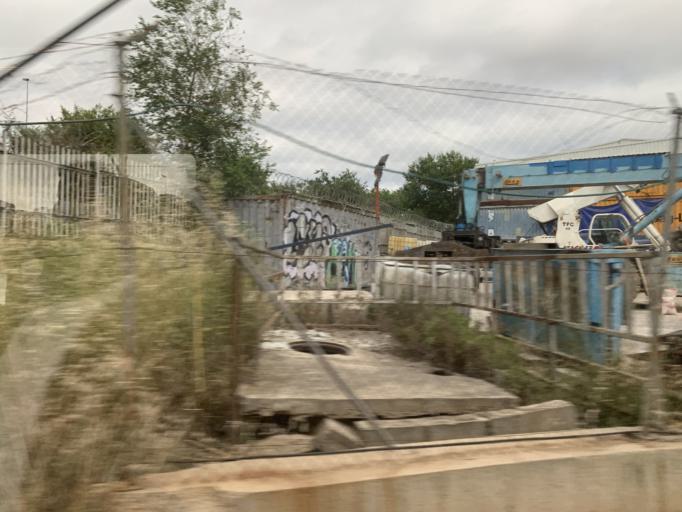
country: ES
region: Catalonia
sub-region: Provincia de Barcelona
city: L'Hospitalet de Llobregat
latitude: 41.3461
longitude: 2.1148
